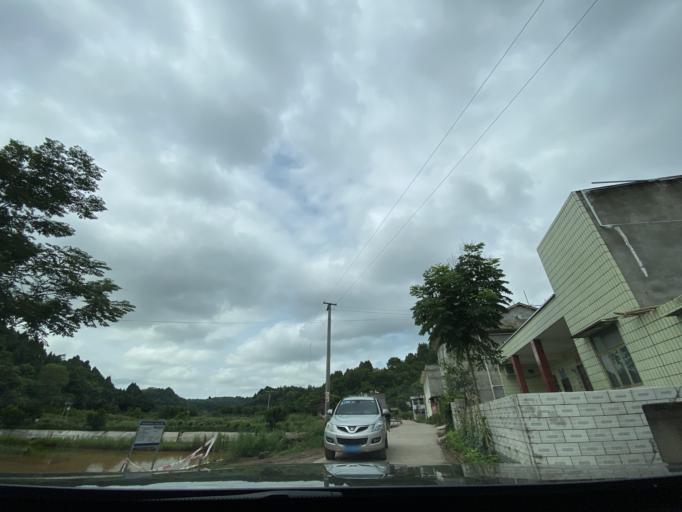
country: CN
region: Sichuan
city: Jiancheng
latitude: 30.4044
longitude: 104.5744
